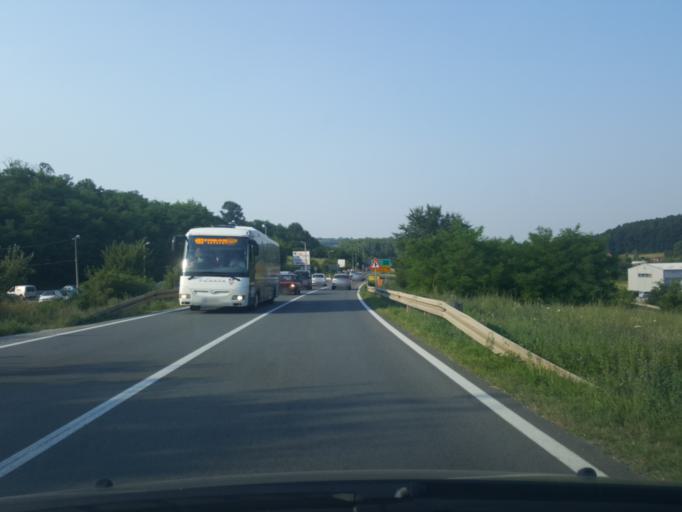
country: RS
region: Central Serbia
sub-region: Belgrade
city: Sopot
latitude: 44.5590
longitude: 20.6677
